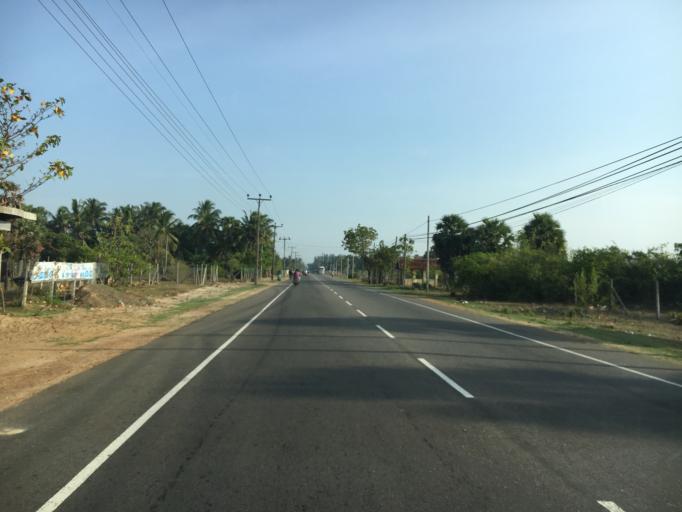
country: LK
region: Eastern Province
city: Eravur Town
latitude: 7.8960
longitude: 81.5365
